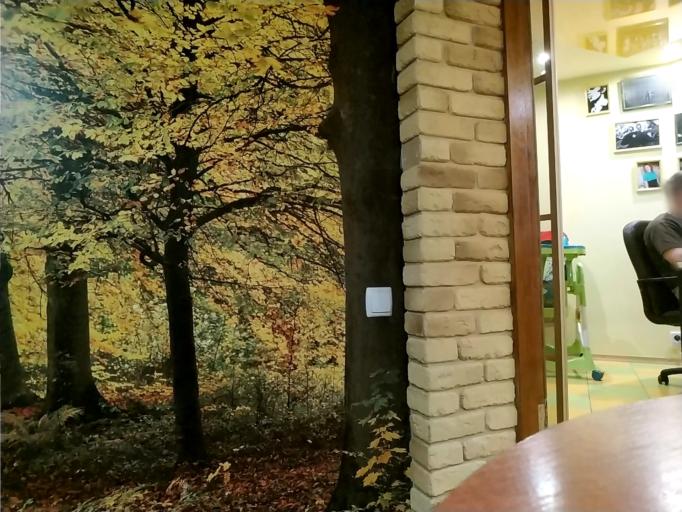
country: RU
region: Tverskaya
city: Zapadnaya Dvina
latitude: 56.3295
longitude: 31.8931
